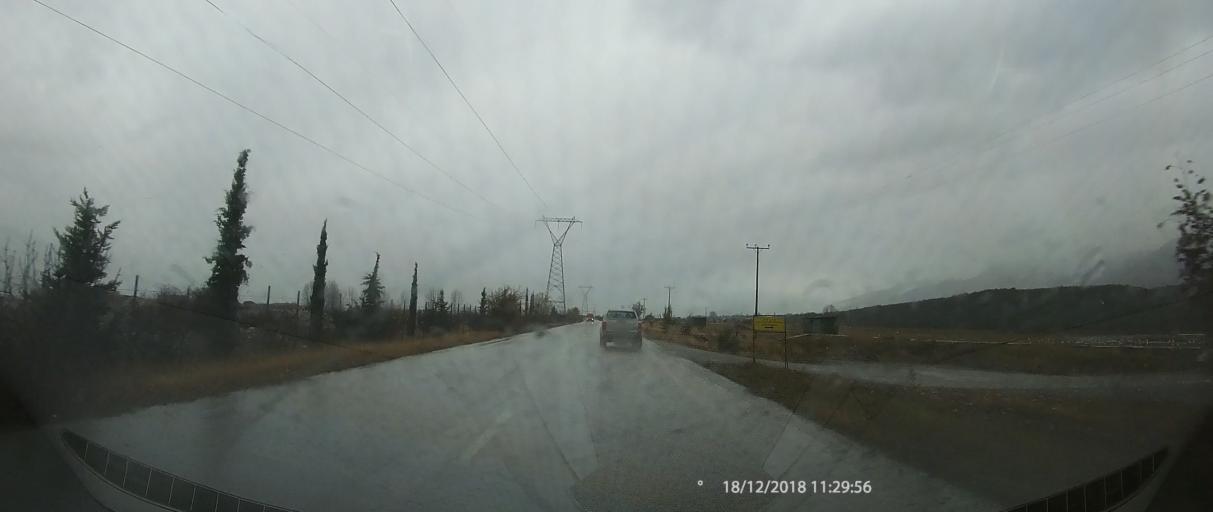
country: GR
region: Central Macedonia
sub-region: Nomos Pierias
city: Litochoro
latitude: 40.1305
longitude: 22.5221
